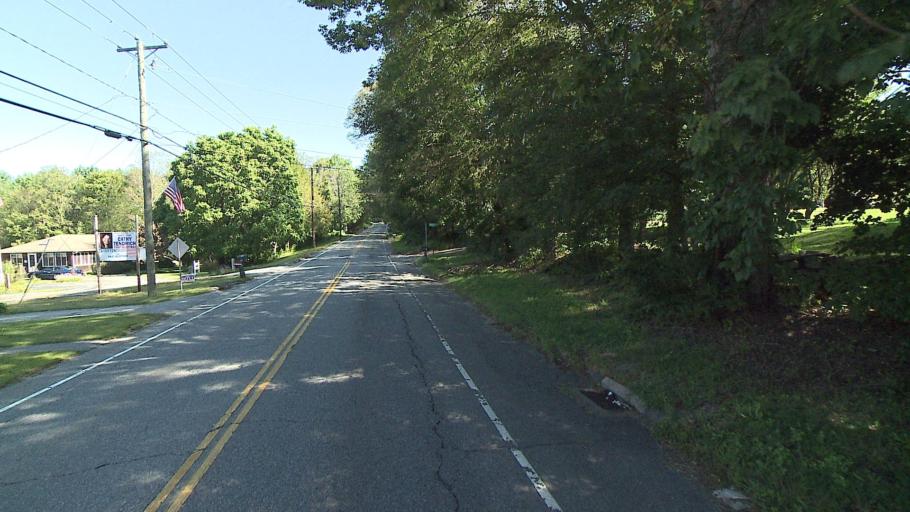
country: US
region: Connecticut
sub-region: Windham County
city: Plainfield
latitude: 41.6895
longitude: -71.9124
